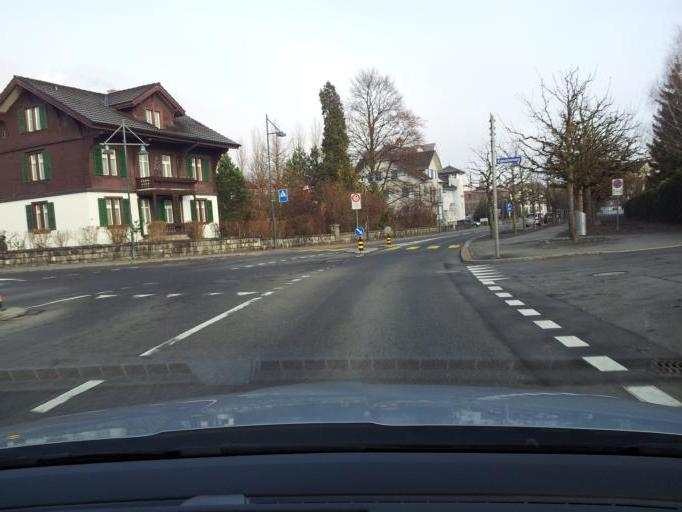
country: CH
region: Obwalden
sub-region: Obwalden
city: Sarnen
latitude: 46.8925
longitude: 8.2447
